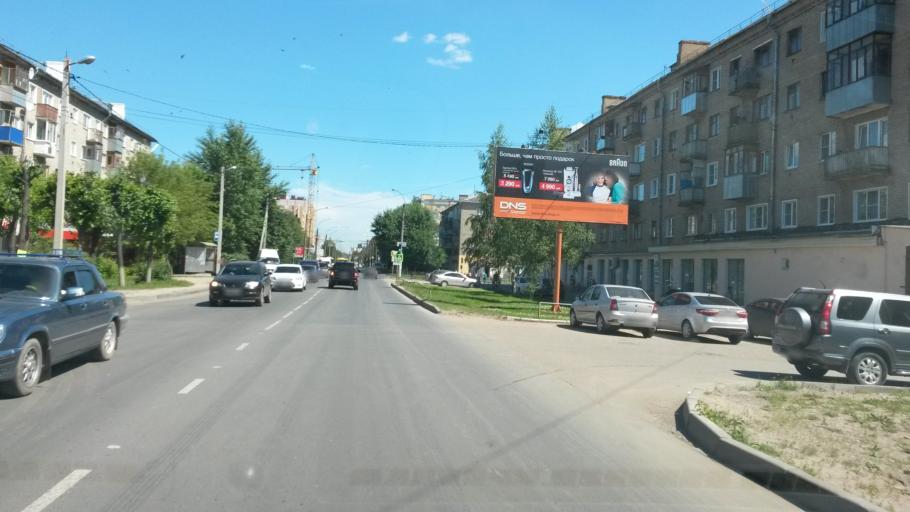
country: RU
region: Ivanovo
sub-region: Gorod Ivanovo
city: Ivanovo
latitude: 56.9835
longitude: 40.9594
